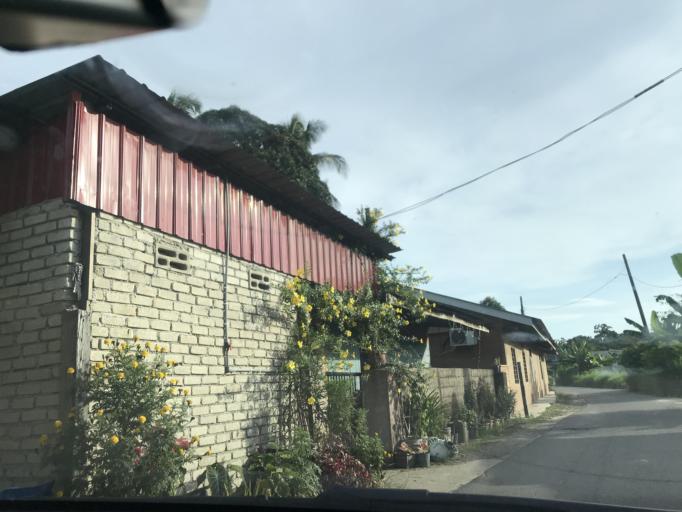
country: MY
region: Kelantan
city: Kota Bharu
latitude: 6.1353
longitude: 102.2239
